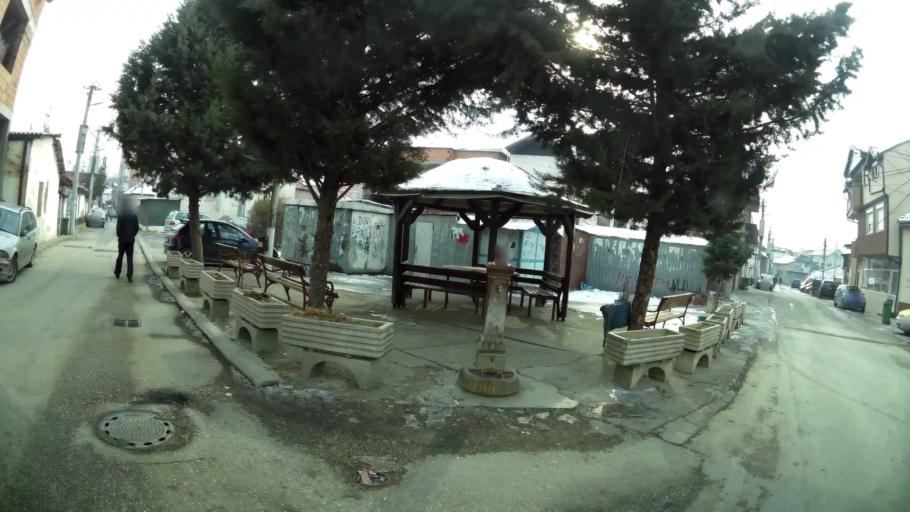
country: MK
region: Cair
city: Cair
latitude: 42.0087
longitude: 21.4402
